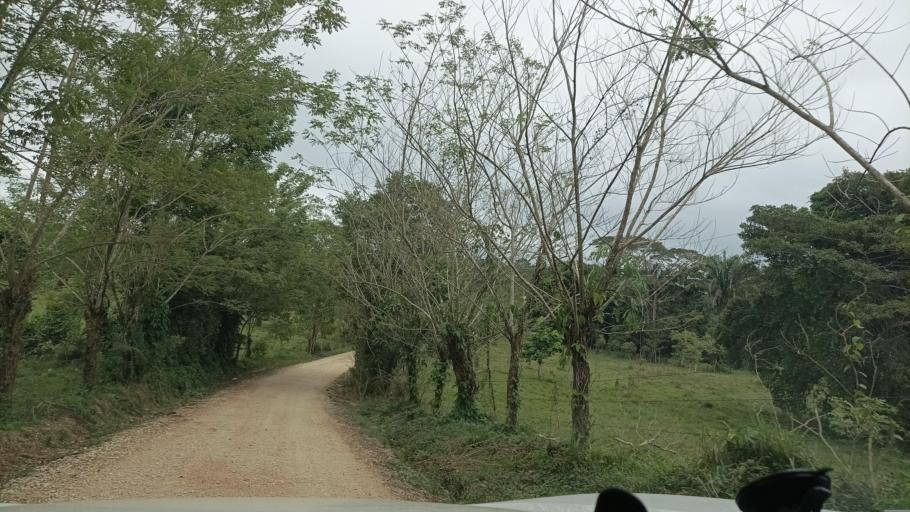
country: MX
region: Veracruz
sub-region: Uxpanapa
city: Poblado Cinco
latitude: 17.4813
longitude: -94.5722
